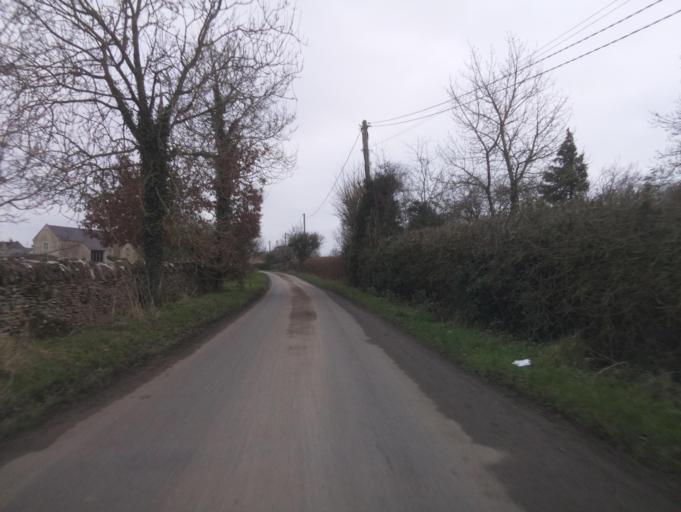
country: GB
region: England
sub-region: Wiltshire
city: Nettleton
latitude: 51.5062
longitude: -2.2662
